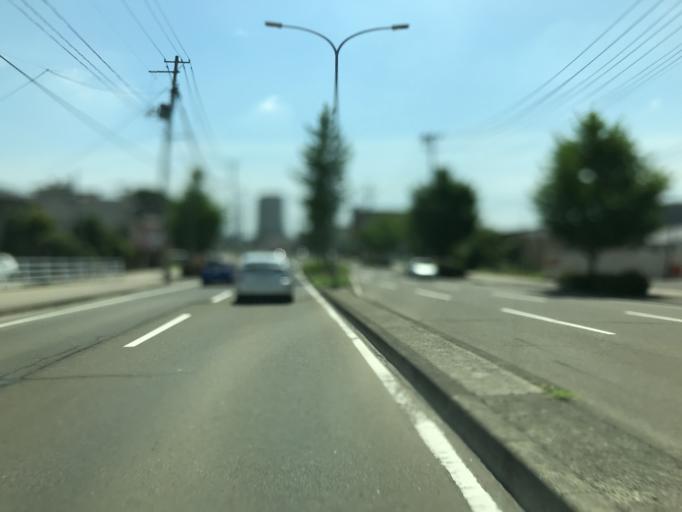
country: JP
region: Miyagi
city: Sendai-shi
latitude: 38.2733
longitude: 140.8903
